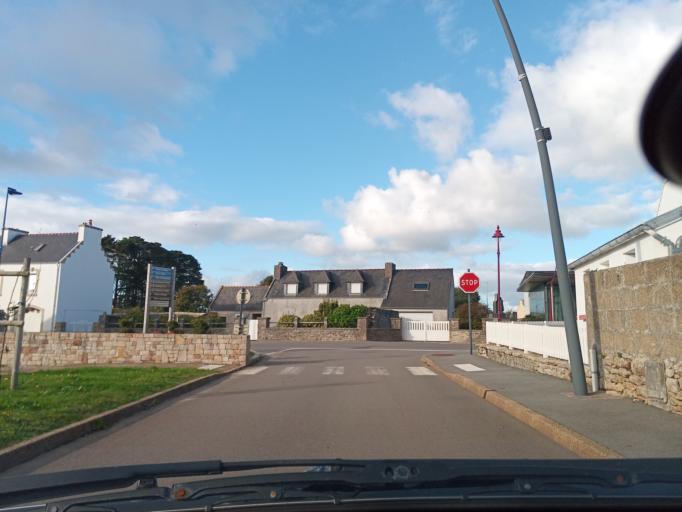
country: FR
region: Brittany
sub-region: Departement du Finistere
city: Plouhinec
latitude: 48.0143
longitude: -4.4884
